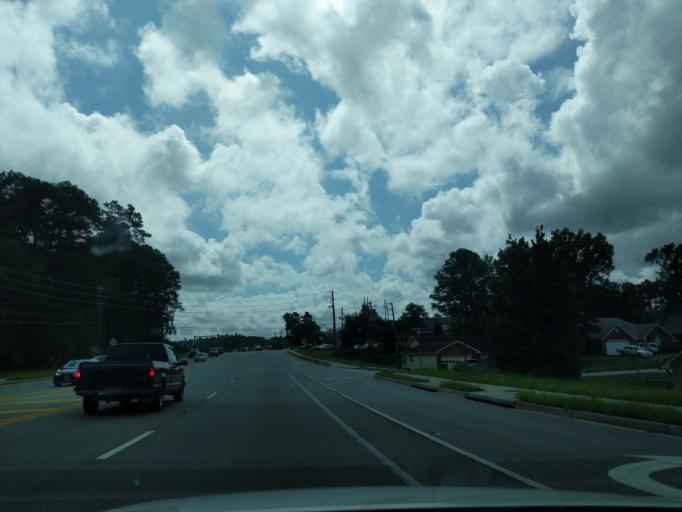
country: US
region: Georgia
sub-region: Columbia County
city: Evans
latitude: 33.5511
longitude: -82.1538
